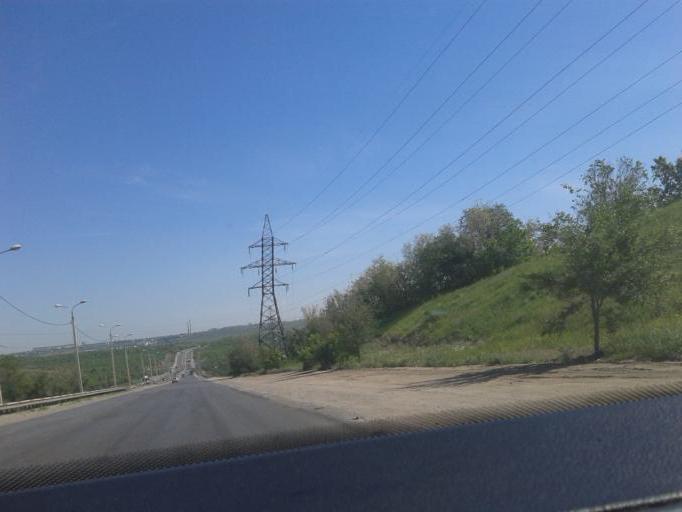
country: RU
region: Volgograd
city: Volgograd
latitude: 48.7100
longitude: 44.4424
